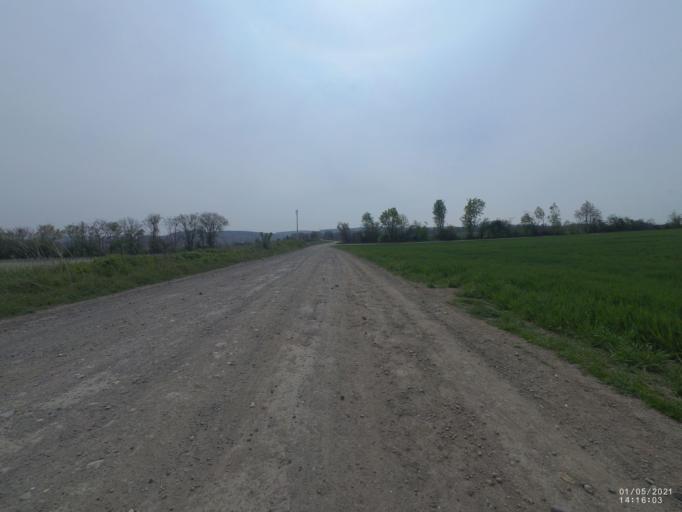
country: DE
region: Rheinland-Pfalz
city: Bassenheim
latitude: 50.3718
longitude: 7.4600
